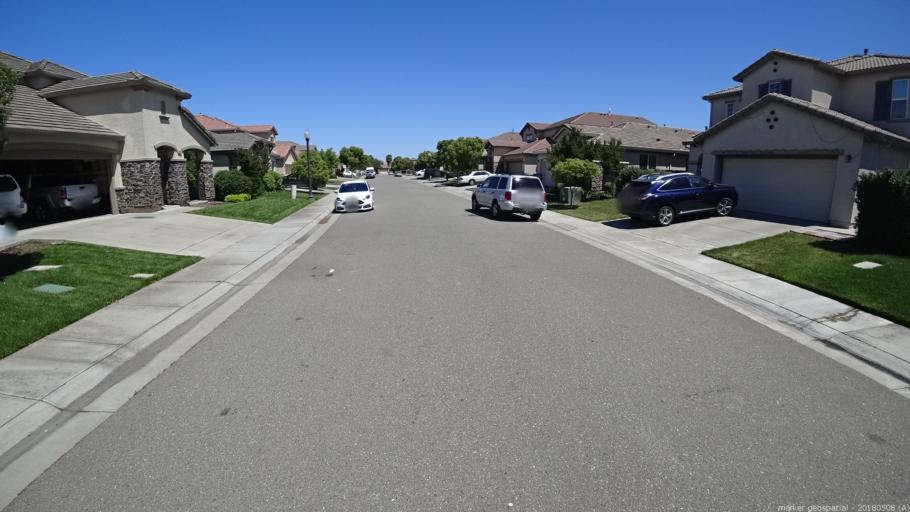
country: US
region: California
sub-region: Sacramento County
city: Elverta
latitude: 38.6787
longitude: -121.5377
